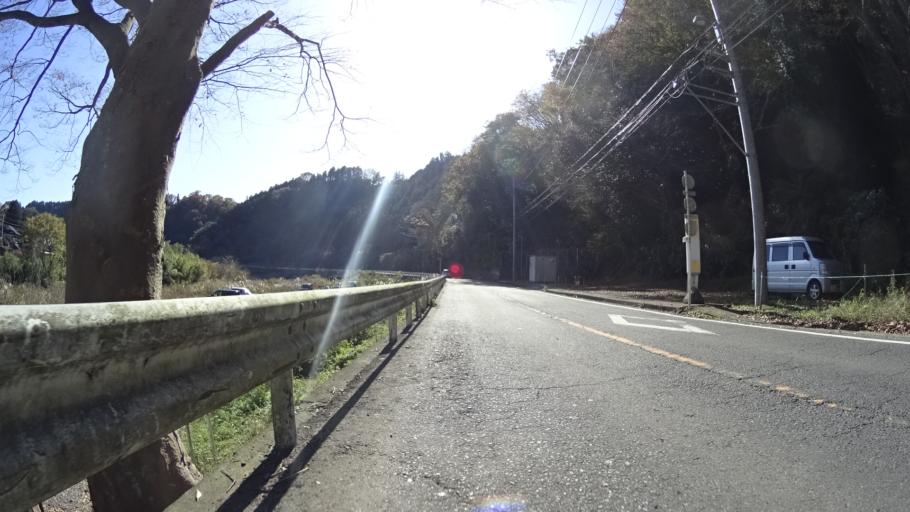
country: JP
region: Kanagawa
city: Zama
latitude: 35.5392
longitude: 139.2780
